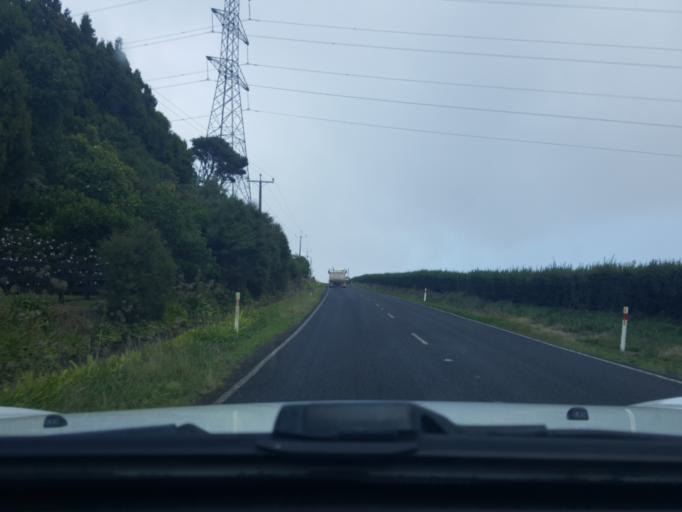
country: NZ
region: Auckland
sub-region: Auckland
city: Pukekohe East
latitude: -37.3076
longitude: 174.9981
